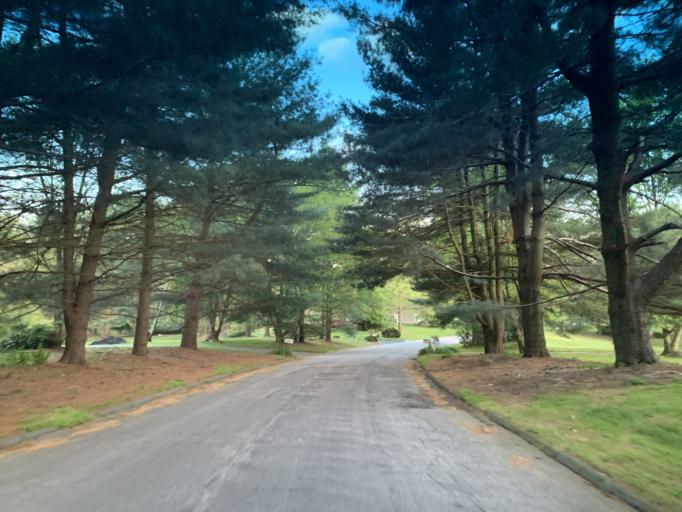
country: US
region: Pennsylvania
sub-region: York County
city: Susquehanna Trails
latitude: 39.6895
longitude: -76.3515
